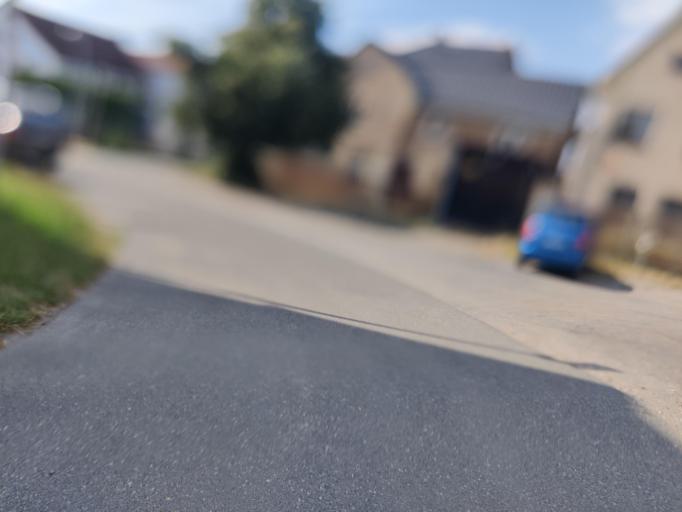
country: DE
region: Thuringia
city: Fockendorf
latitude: 51.0438
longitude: 12.4582
